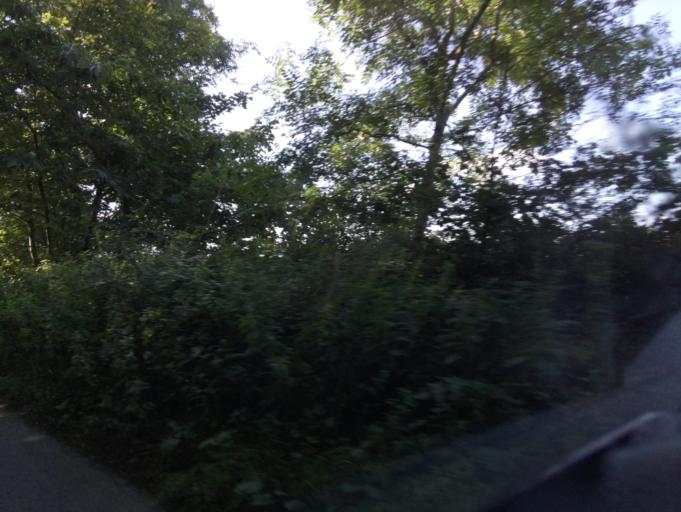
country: GB
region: England
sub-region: Devon
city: Tavistock
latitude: 50.5522
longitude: -4.1068
